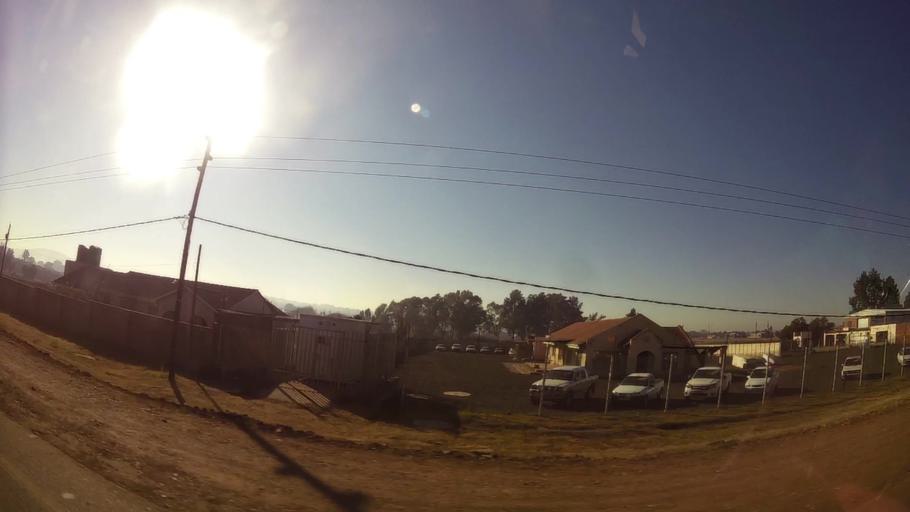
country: ZA
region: Gauteng
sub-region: City of Tshwane Metropolitan Municipality
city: Centurion
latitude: -25.8554
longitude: 28.1086
